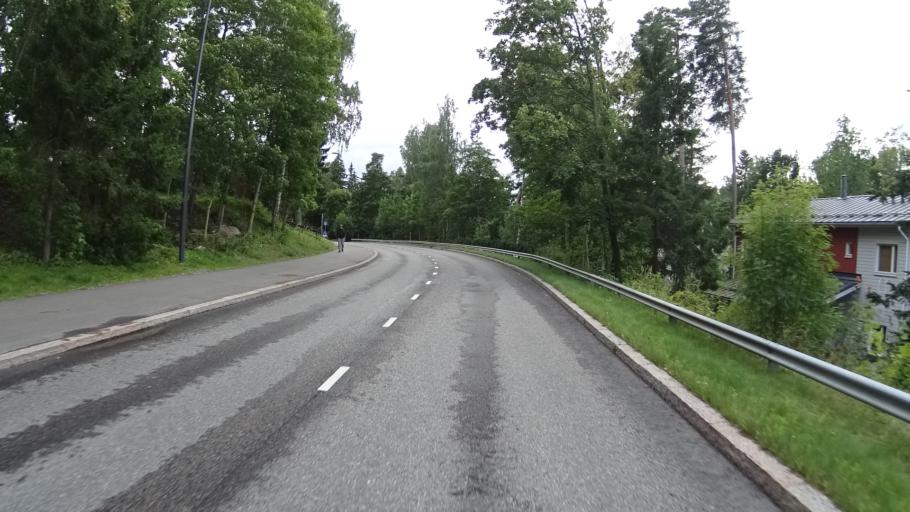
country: FI
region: Uusimaa
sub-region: Helsinki
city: Kauniainen
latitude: 60.2154
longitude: 24.7399
